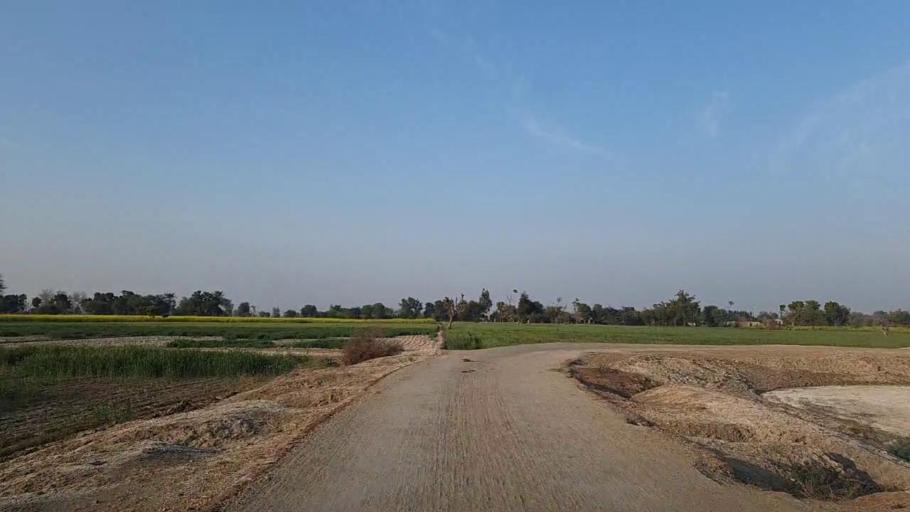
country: PK
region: Sindh
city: Jam Sahib
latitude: 26.3902
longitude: 68.5404
